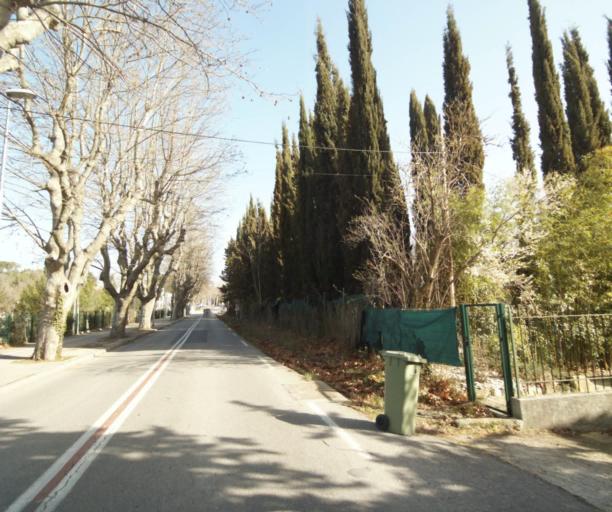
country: FR
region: Provence-Alpes-Cote d'Azur
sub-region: Departement des Bouches-du-Rhone
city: Aix-en-Provence
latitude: 43.5544
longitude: 5.4589
